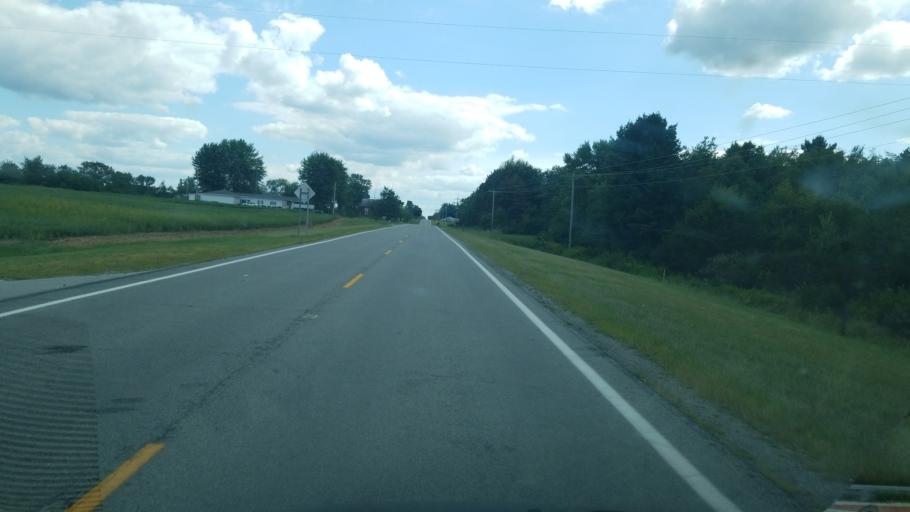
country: US
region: Ohio
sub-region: Allen County
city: Lima
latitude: 40.6574
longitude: -83.9756
